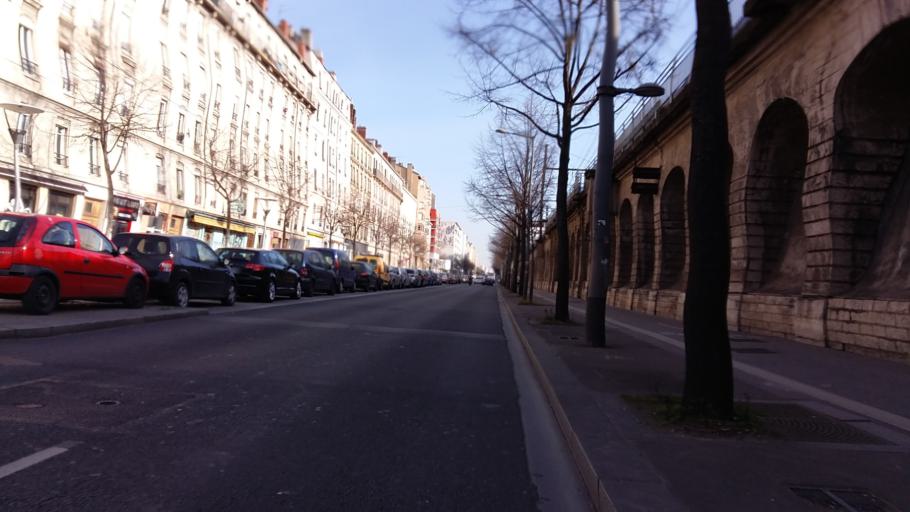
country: FR
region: Rhone-Alpes
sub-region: Departement du Rhone
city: Lyon
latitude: 45.7446
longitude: 4.8438
